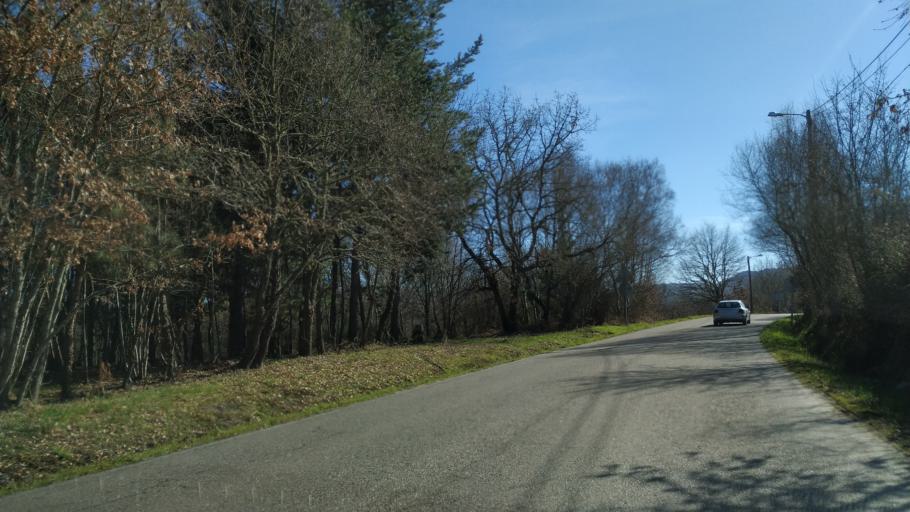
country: ES
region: Galicia
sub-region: Provincia de Ourense
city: Allariz
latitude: 42.2012
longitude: -7.8076
